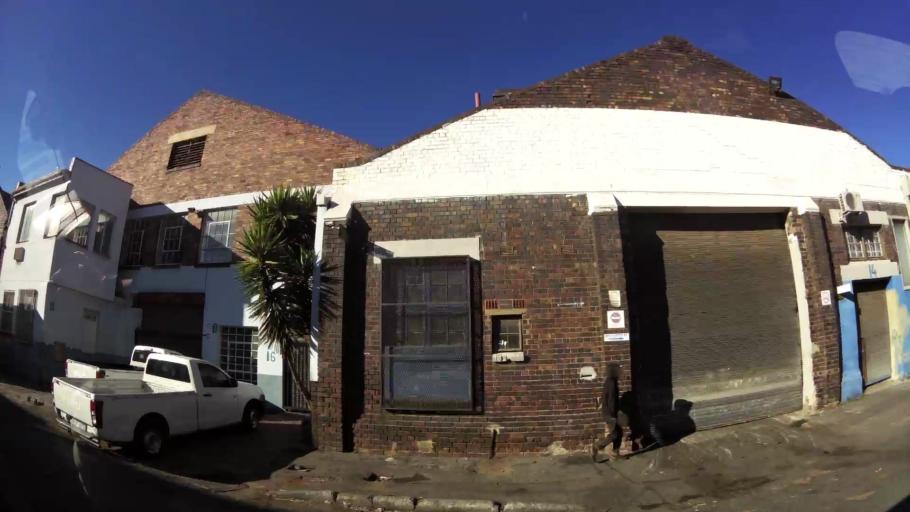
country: ZA
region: Gauteng
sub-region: City of Johannesburg Metropolitan Municipality
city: Johannesburg
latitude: -26.2016
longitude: 28.0266
